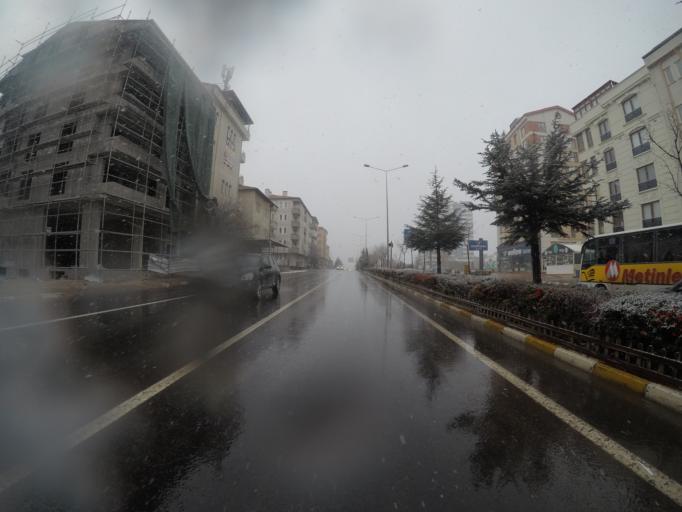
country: TR
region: Nevsehir
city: Nevsehir
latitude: 38.6305
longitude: 34.7342
